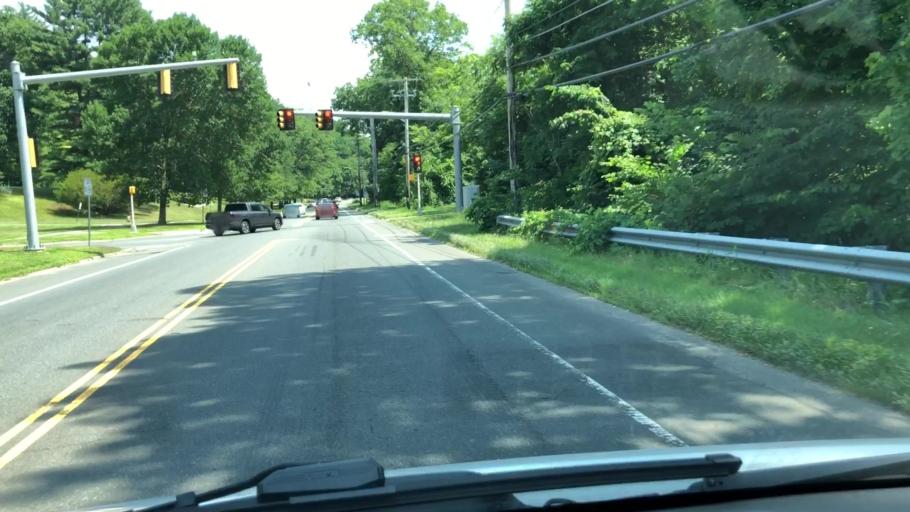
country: US
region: Massachusetts
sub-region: Hampshire County
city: Northampton
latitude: 42.3476
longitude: -72.6867
